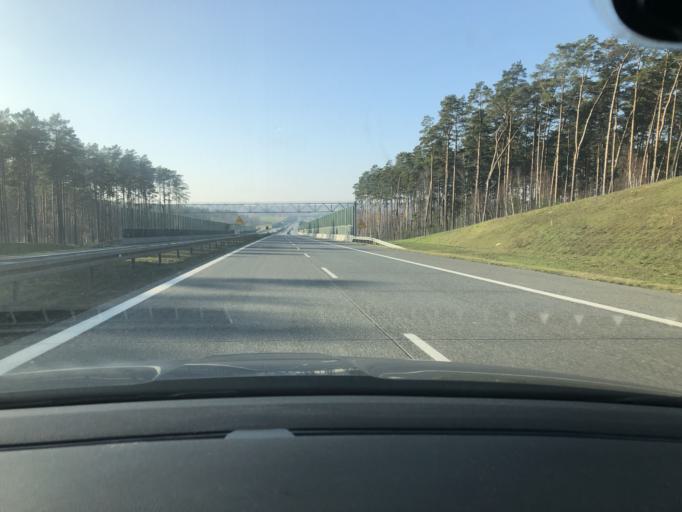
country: PL
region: Lubusz
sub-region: Powiat swiebodzinski
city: Lubrza
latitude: 52.3166
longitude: 15.4560
